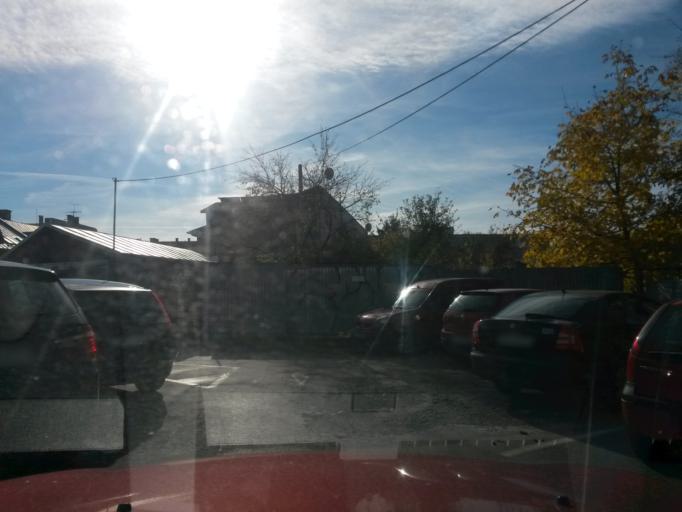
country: SK
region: Presovsky
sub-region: Okres Presov
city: Presov
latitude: 49.0017
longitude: 21.2327
